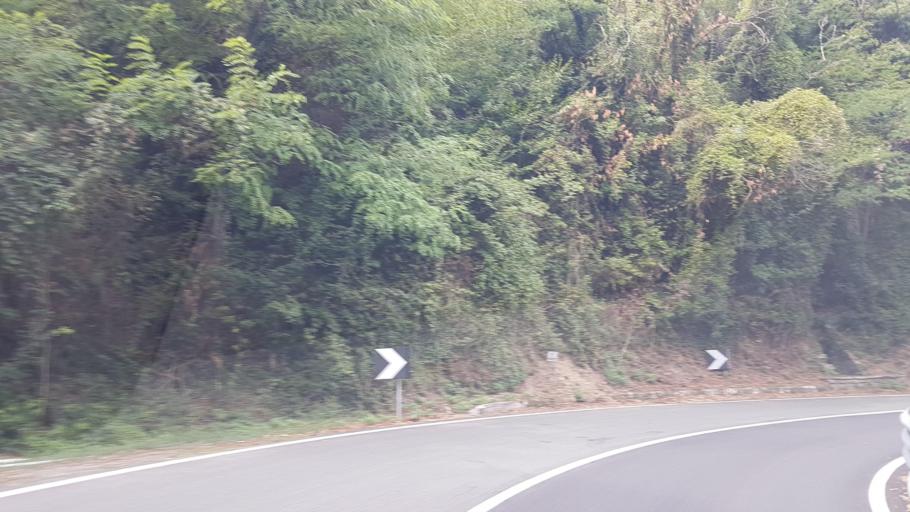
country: IT
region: Liguria
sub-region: Provincia di Genova
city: Moneglia
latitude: 44.2564
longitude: 9.4734
